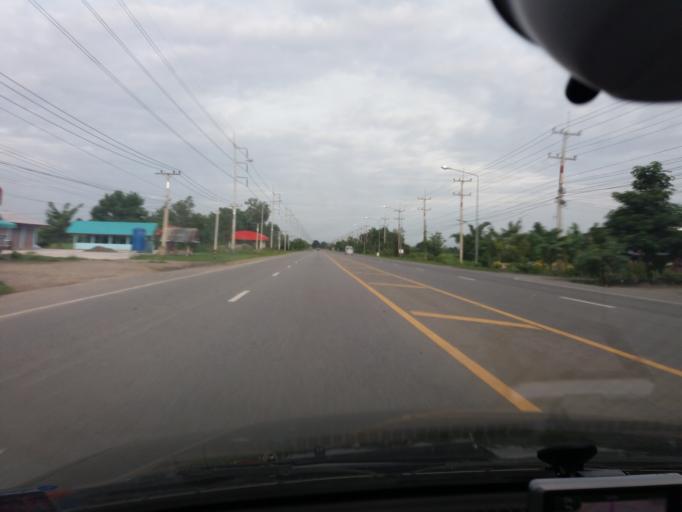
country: TH
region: Kanchanaburi
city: Huai Krachao
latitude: 14.3345
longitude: 99.7769
